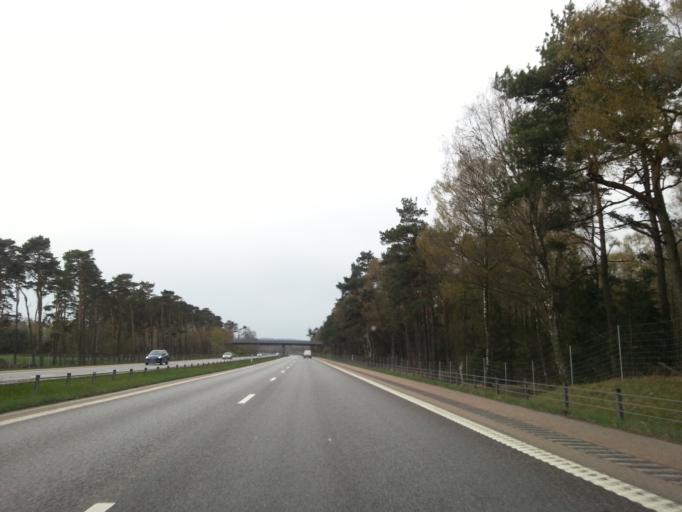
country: SE
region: Halland
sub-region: Laholms Kommun
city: Mellbystrand
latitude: 56.4804
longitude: 12.9464
